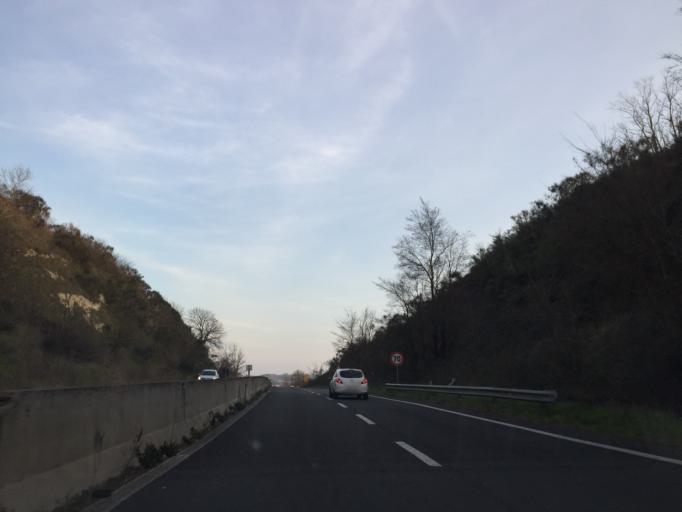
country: IT
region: Latium
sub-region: Citta metropolitana di Roma Capitale
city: Campagnano di Roma
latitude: 42.1364
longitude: 12.3527
